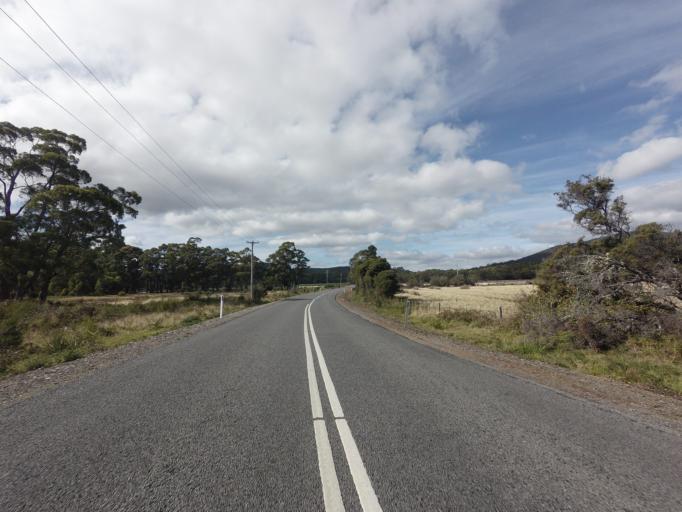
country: AU
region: Tasmania
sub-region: Clarence
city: Sandford
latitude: -43.1316
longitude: 147.7927
